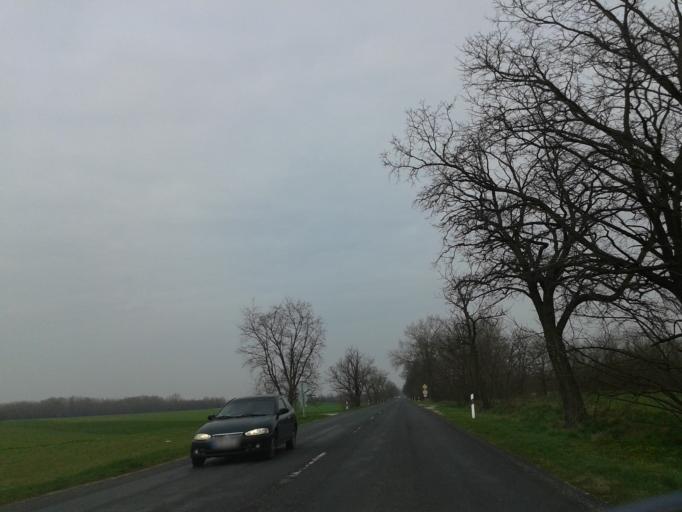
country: HU
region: Komarom-Esztergom
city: Acs
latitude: 47.7301
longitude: 17.9849
